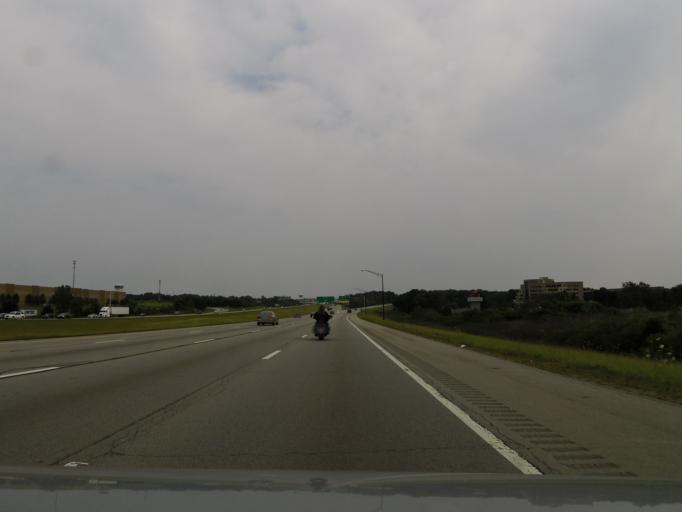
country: US
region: Ohio
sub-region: Warren County
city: Five Points
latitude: 39.6106
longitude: -84.2333
